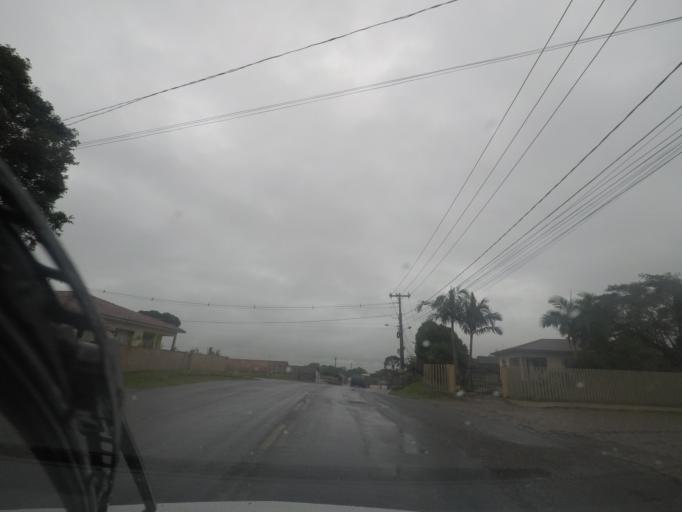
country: BR
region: Parana
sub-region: Quatro Barras
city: Quatro Barras
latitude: -25.3749
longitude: -49.1110
